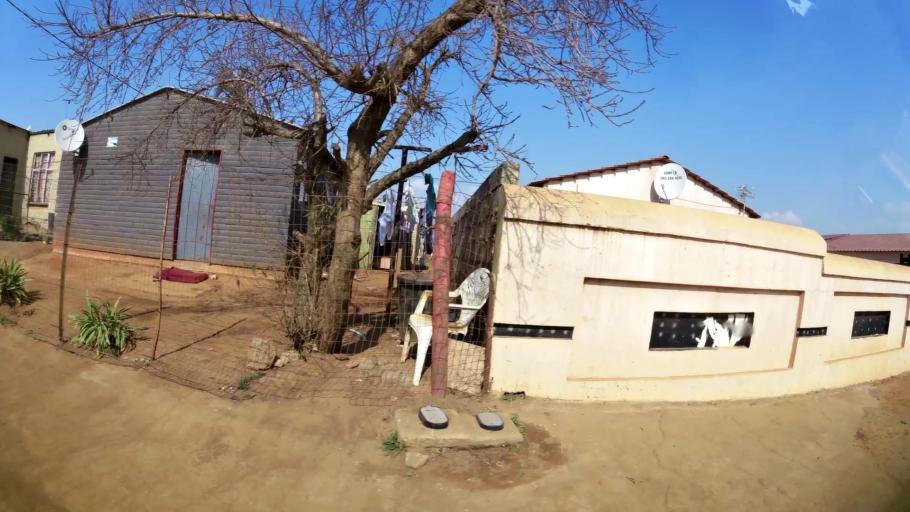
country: ZA
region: Gauteng
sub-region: Ekurhuleni Metropolitan Municipality
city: Springs
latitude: -26.1155
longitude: 28.4784
